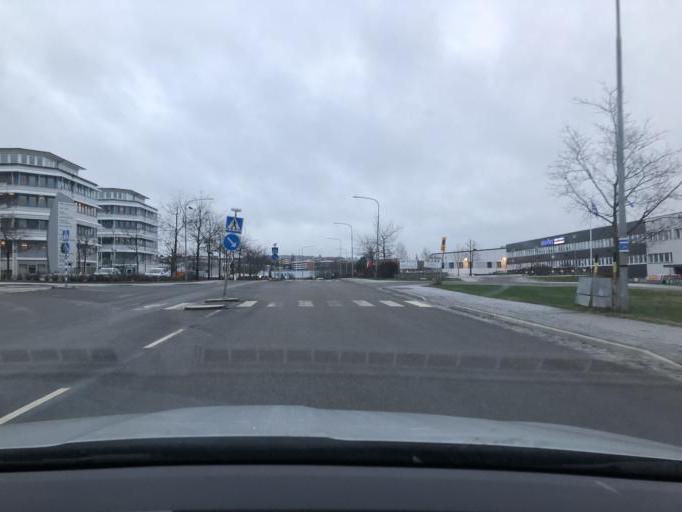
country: SE
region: Stockholm
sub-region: Jarfalla Kommun
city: Jakobsberg
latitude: 59.3894
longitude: 17.8788
